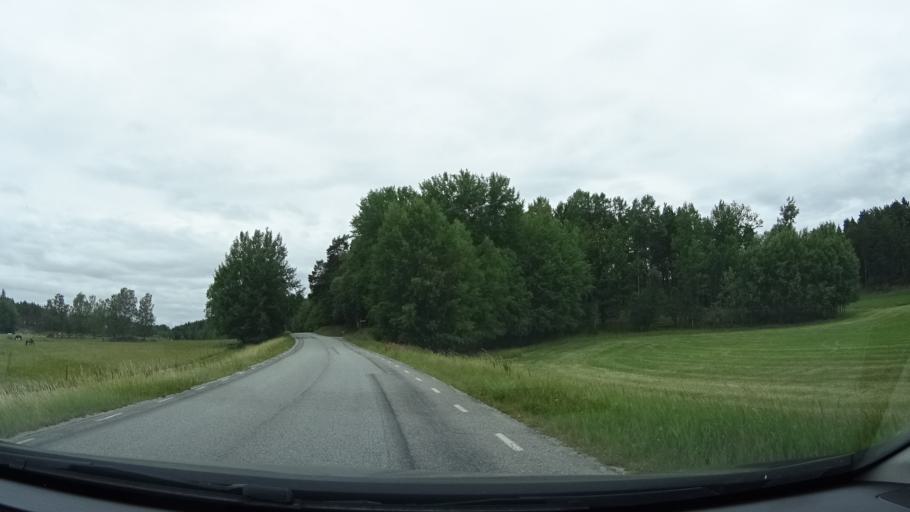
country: SE
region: Stockholm
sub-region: Varmdo Kommun
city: Hemmesta
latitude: 59.3586
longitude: 18.4884
